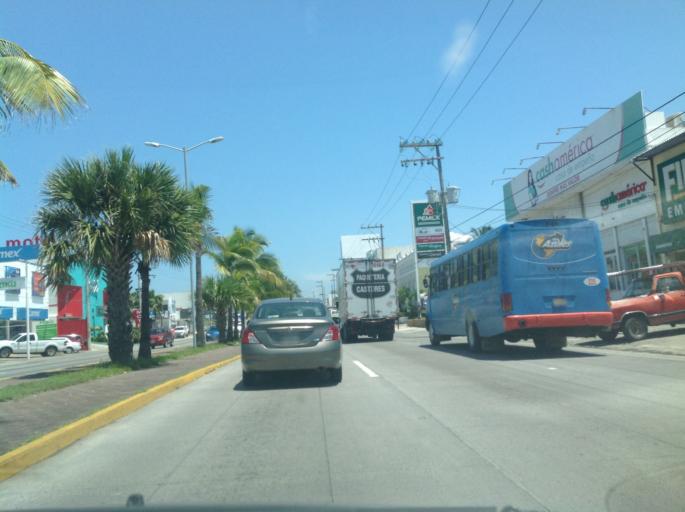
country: MX
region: Veracruz
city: Boca del Rio
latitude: 19.1415
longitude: -96.1193
